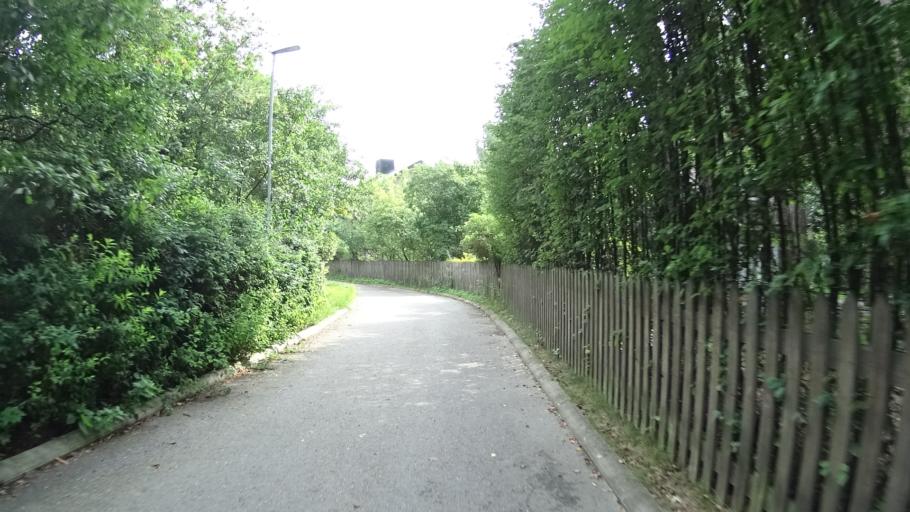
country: FI
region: Uusimaa
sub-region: Helsinki
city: Teekkarikylae
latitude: 60.2276
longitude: 24.8474
